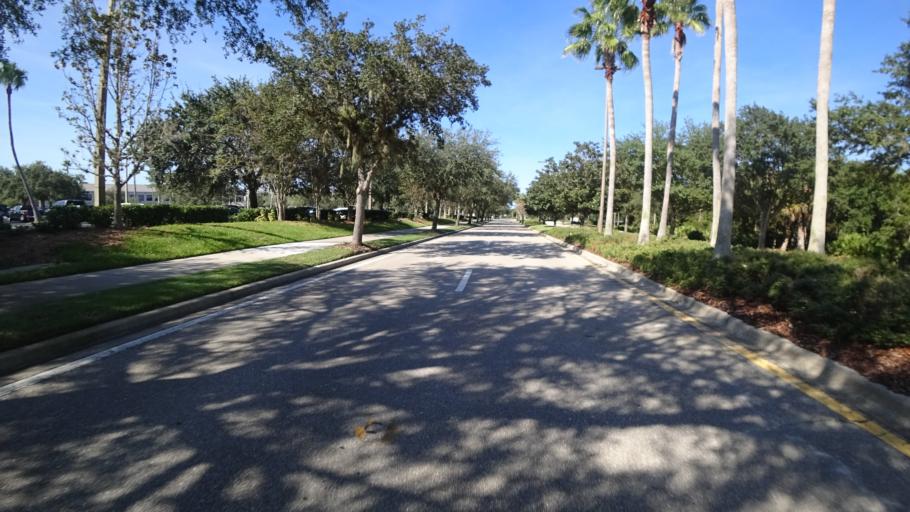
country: US
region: Florida
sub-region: Sarasota County
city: The Meadows
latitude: 27.3963
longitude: -82.4479
